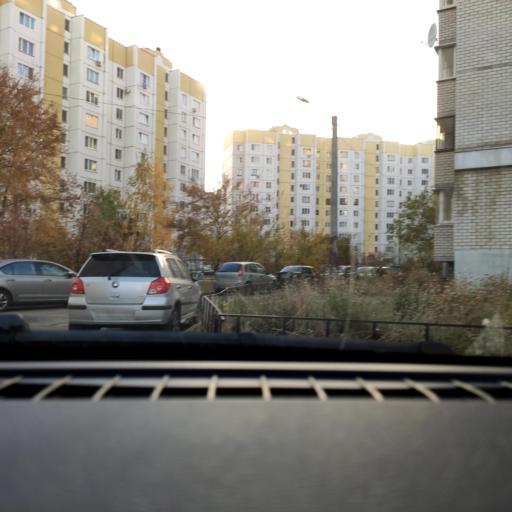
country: RU
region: Voronezj
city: Somovo
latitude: 51.6897
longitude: 39.2834
